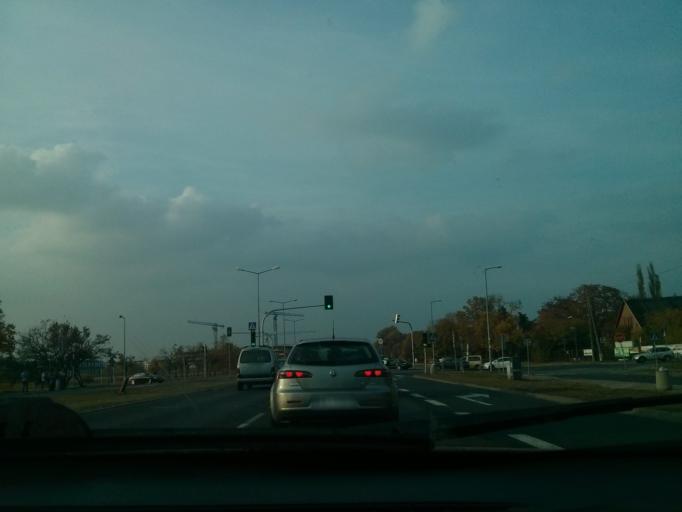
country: PL
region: Masovian Voivodeship
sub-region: Warszawa
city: Wilanow
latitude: 52.1589
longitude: 21.0876
